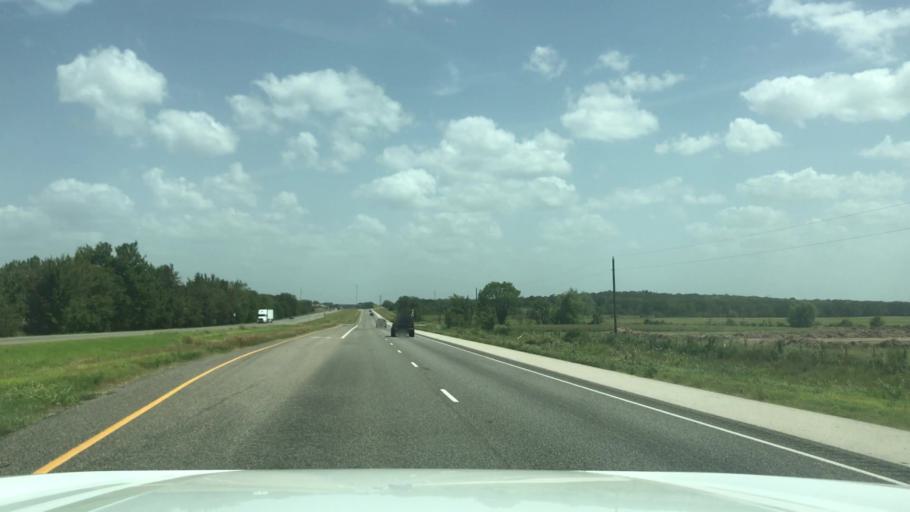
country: US
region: Texas
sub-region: Robertson County
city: Hearne
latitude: 30.9176
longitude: -96.6200
